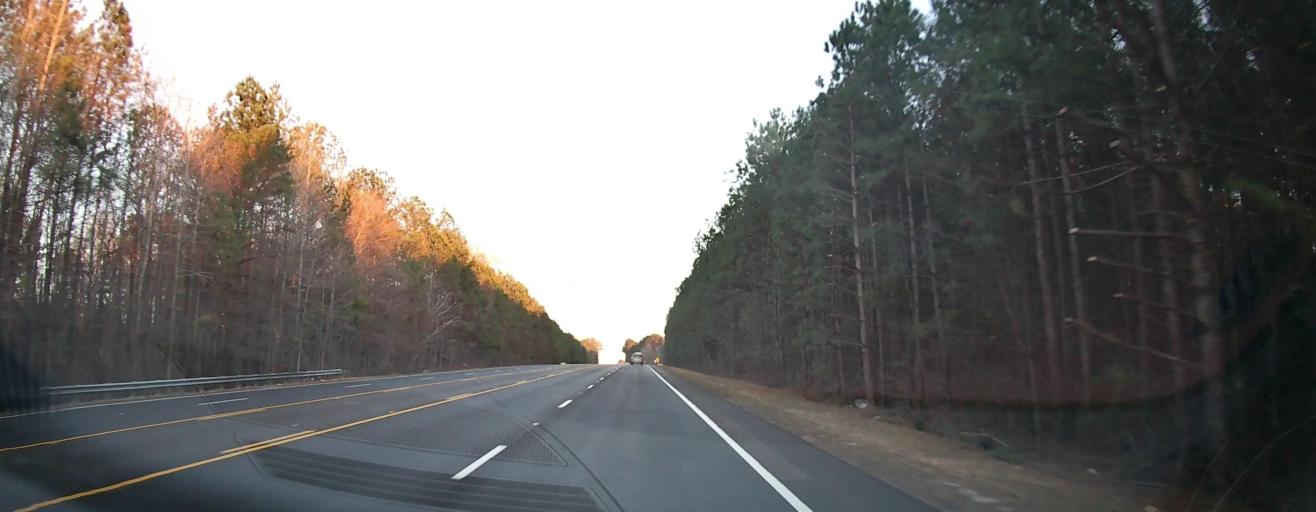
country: US
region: Georgia
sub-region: Clayton County
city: Riverdale
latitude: 33.5513
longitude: -84.4742
